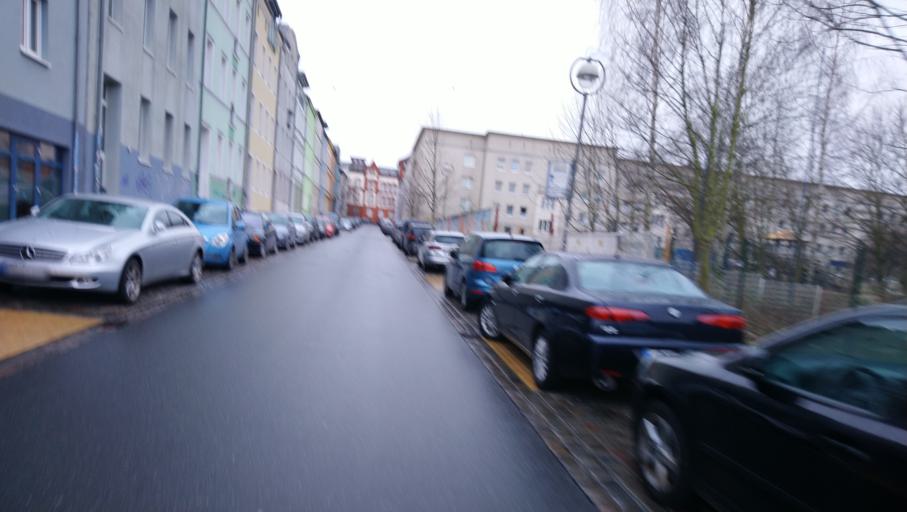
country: DE
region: Mecklenburg-Vorpommern
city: Rostock
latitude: 54.0916
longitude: 12.1273
